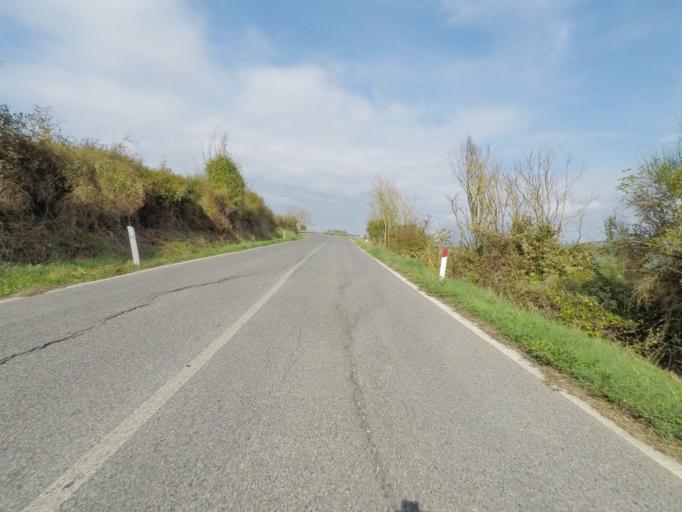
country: IT
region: Tuscany
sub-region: Provincia di Siena
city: Belverde
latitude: 43.3631
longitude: 11.3279
